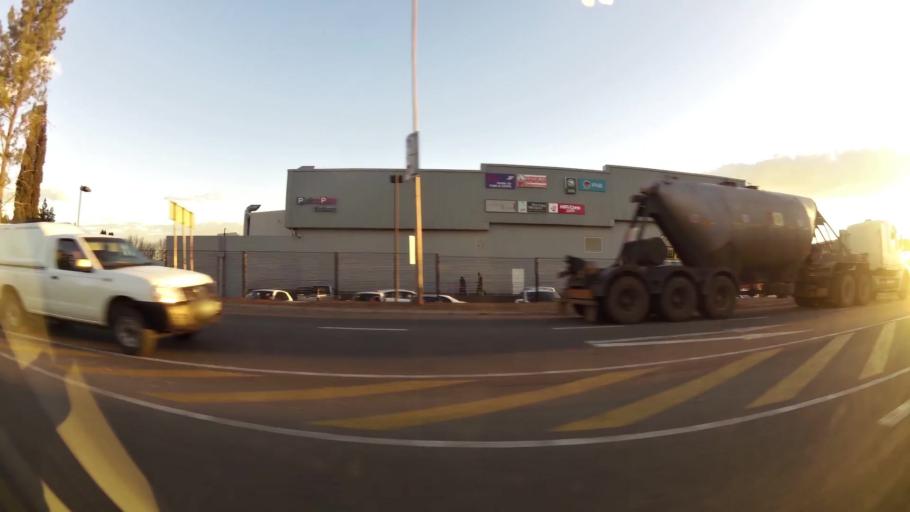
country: ZA
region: North-West
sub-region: Dr Kenneth Kaunda District Municipality
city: Potchefstroom
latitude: -26.7125
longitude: 27.1100
